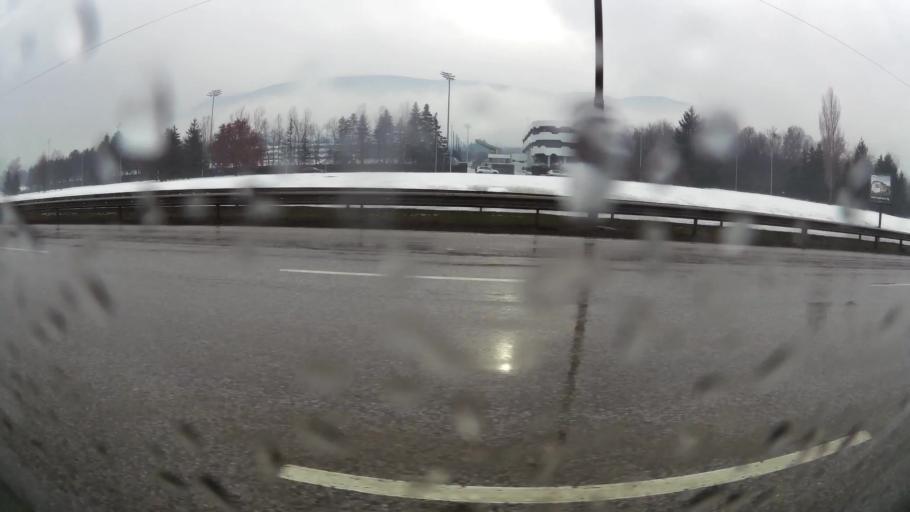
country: BG
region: Sofia-Capital
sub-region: Stolichna Obshtina
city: Sofia
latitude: 42.6555
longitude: 23.2782
